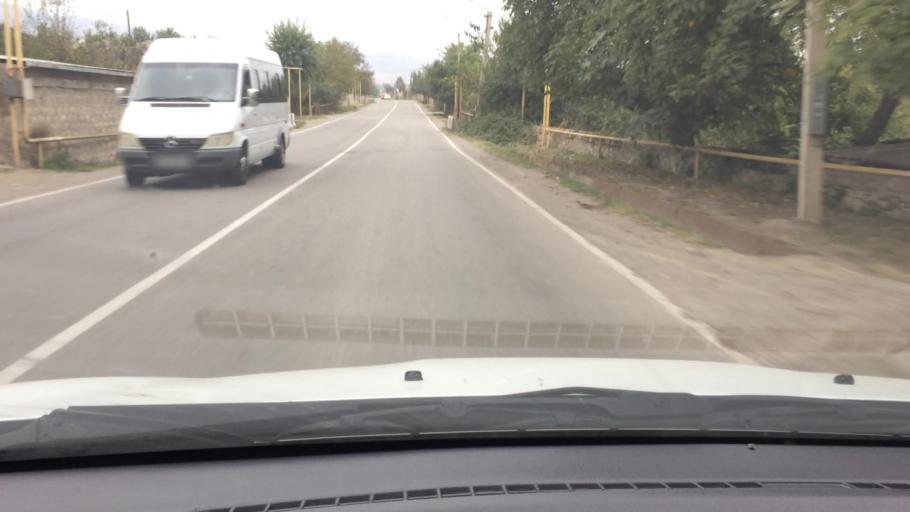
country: AM
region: Tavush
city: Bagratashen
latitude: 41.2389
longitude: 44.8023
